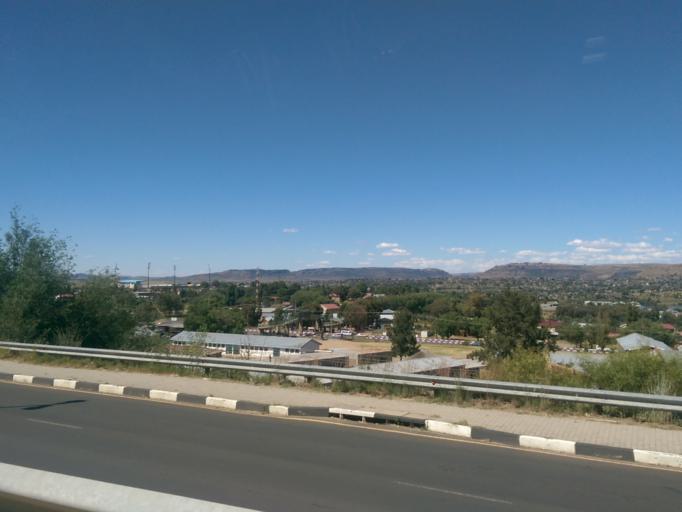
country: LS
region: Maseru
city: Maseru
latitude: -29.3219
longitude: 27.4950
